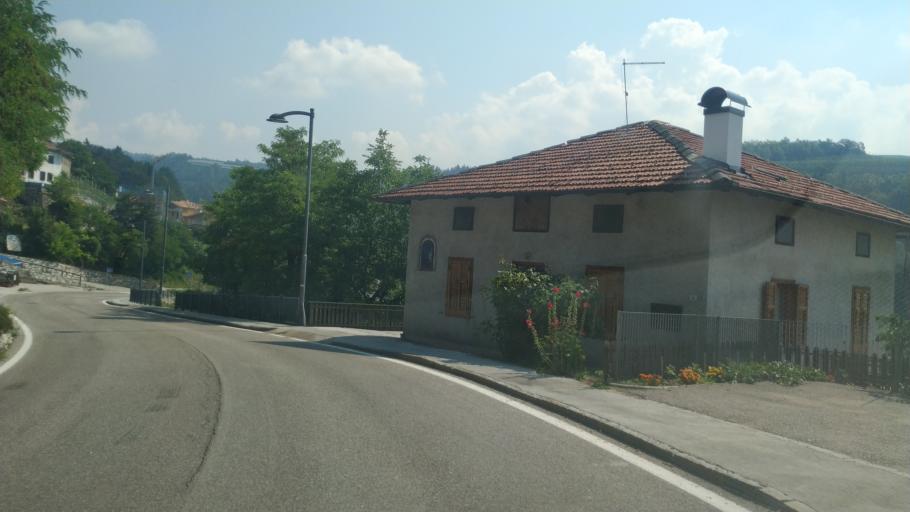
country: IT
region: Trentino-Alto Adige
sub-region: Provincia di Trento
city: Sanzeno
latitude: 46.3641
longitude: 11.0735
